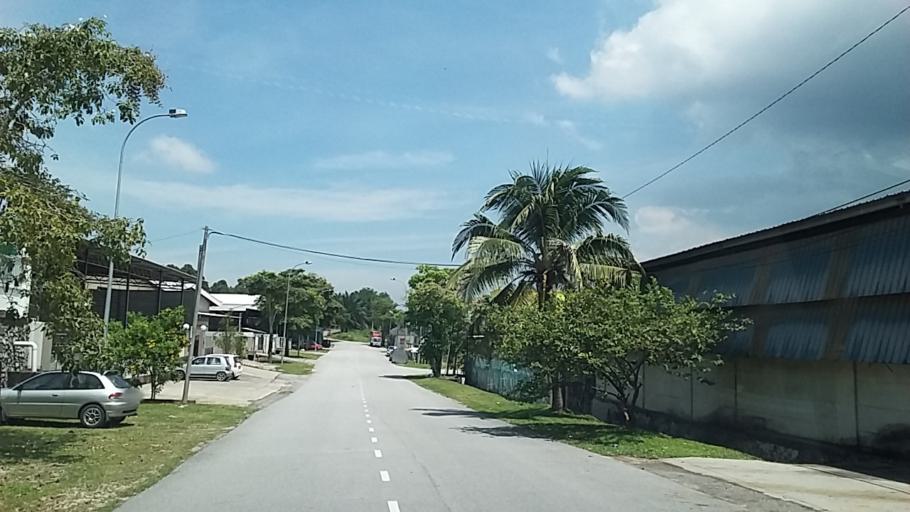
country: MY
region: Johor
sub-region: Daerah Batu Pahat
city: Batu Pahat
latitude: 1.7833
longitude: 102.9672
